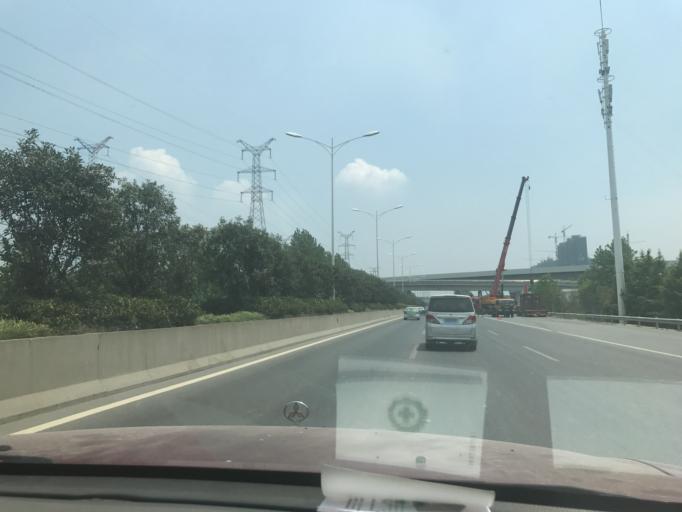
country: CN
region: Hubei
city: Zhanjiaji
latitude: 30.6892
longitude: 114.3338
